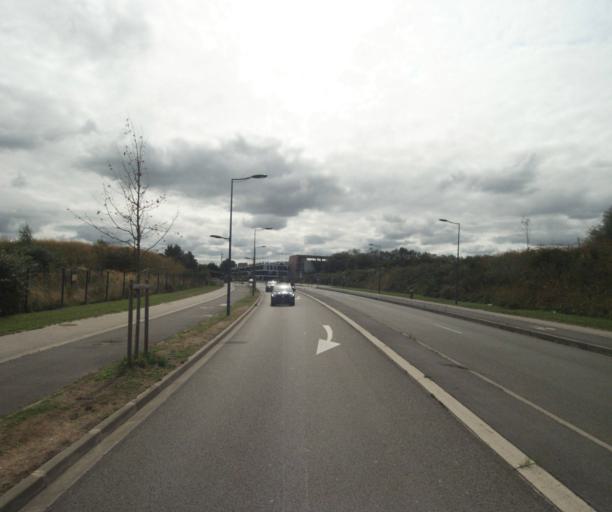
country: FR
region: Nord-Pas-de-Calais
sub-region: Departement du Nord
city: Lezennes
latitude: 50.6095
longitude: 3.1247
